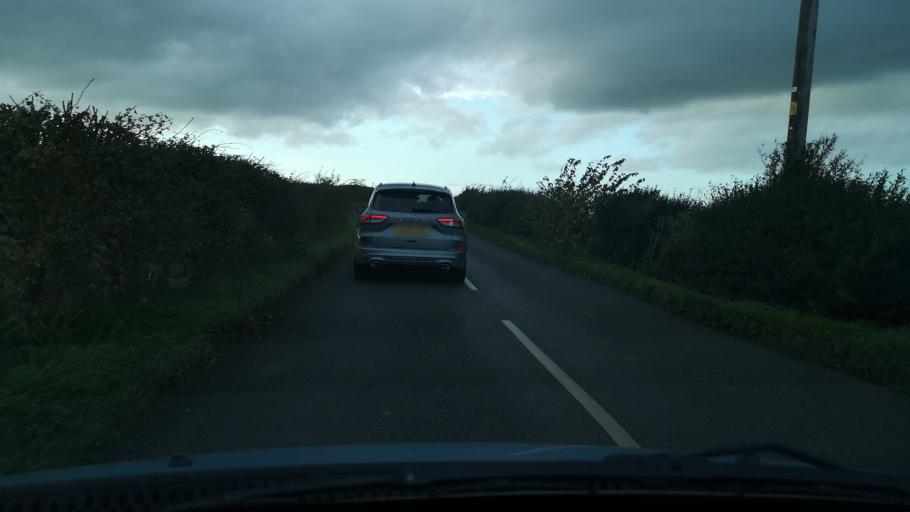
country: GB
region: England
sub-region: Doncaster
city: Norton
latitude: 53.6315
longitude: -1.1914
